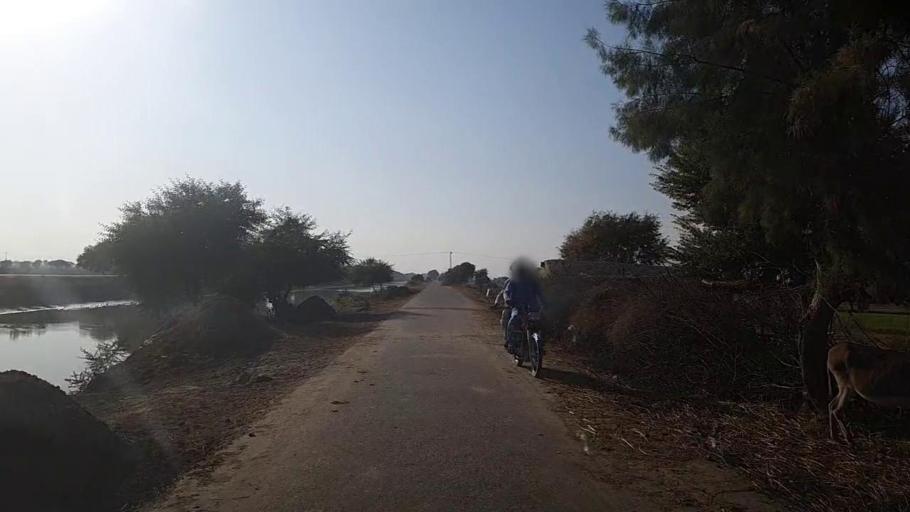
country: PK
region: Sindh
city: Tangwani
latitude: 28.3012
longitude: 68.9410
